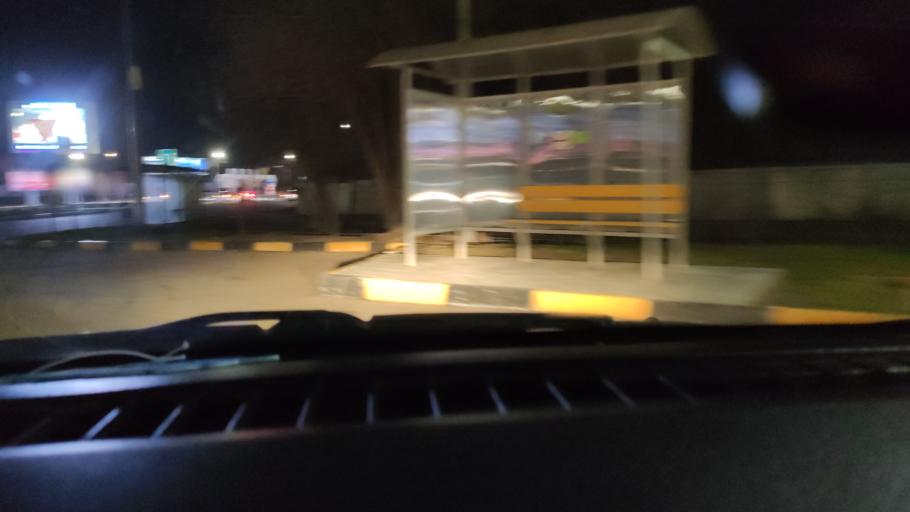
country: RU
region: Saratov
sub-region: Saratovskiy Rayon
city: Saratov
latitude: 51.5564
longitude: 46.0426
